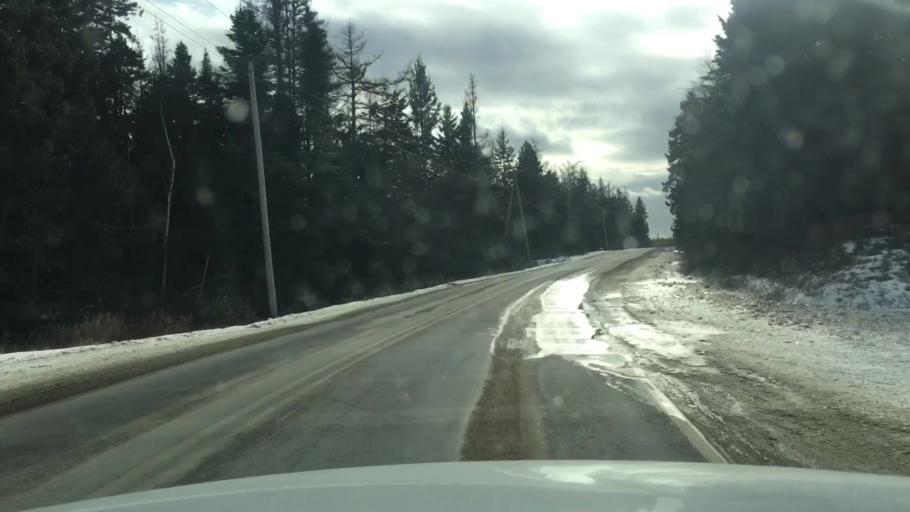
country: US
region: Maine
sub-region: Washington County
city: Jonesport
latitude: 44.6336
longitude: -67.5939
